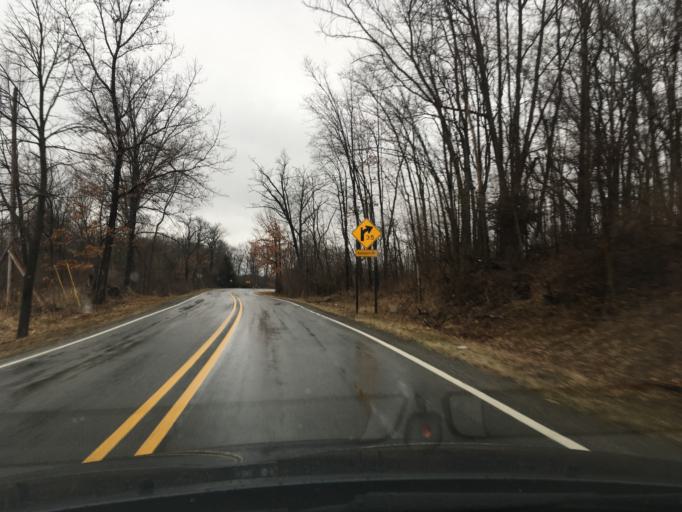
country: US
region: Michigan
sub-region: Washtenaw County
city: Chelsea
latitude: 42.3096
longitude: -84.0916
